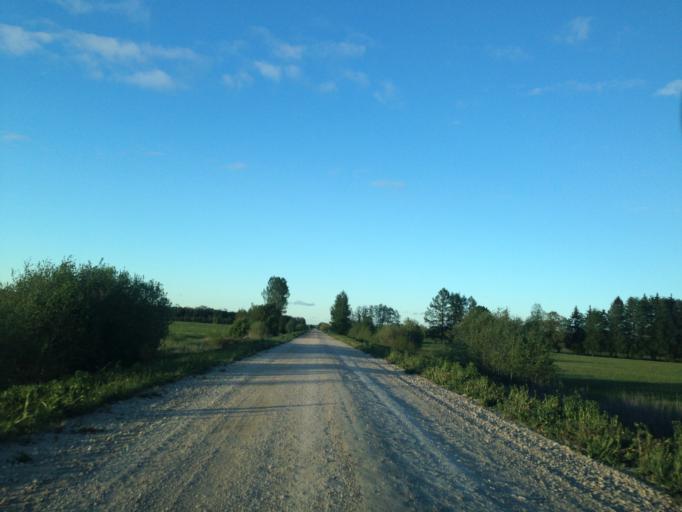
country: EE
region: Raplamaa
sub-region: Maerjamaa vald
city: Marjamaa
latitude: 58.7394
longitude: 24.1660
